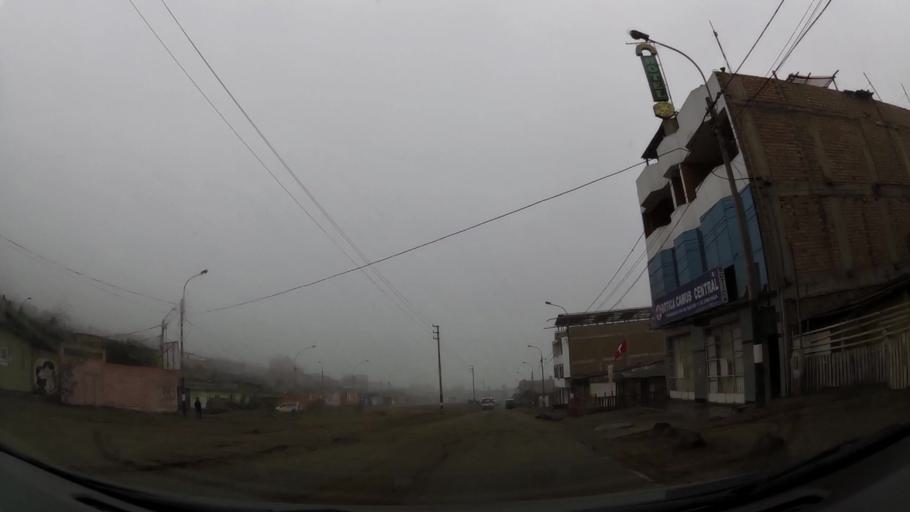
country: PE
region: Lima
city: Ventanilla
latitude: -11.8353
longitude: -77.1383
